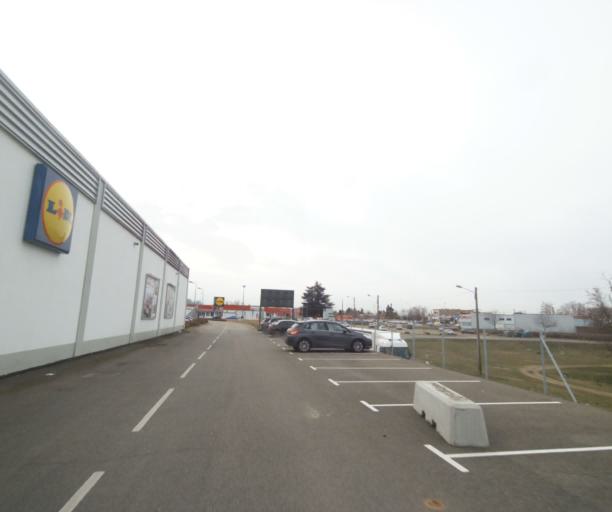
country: FR
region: Rhone-Alpes
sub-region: Departement de la Loire
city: Le Coteau
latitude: 46.0515
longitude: 4.0868
